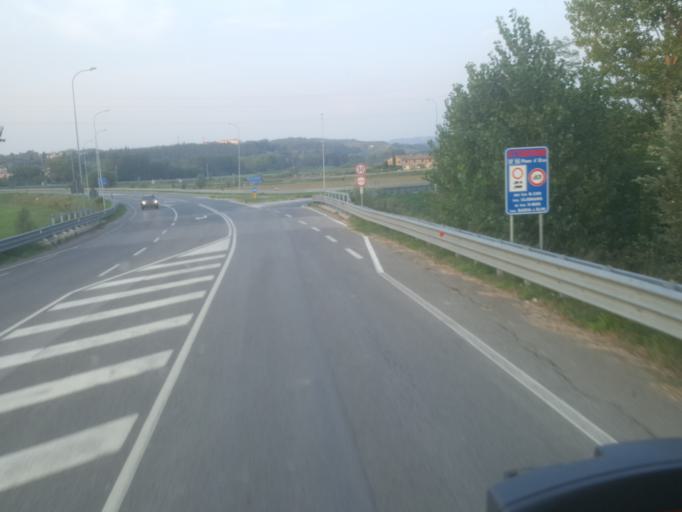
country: IT
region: Tuscany
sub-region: Province of Florence
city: Certaldo
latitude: 43.5304
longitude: 11.0384
